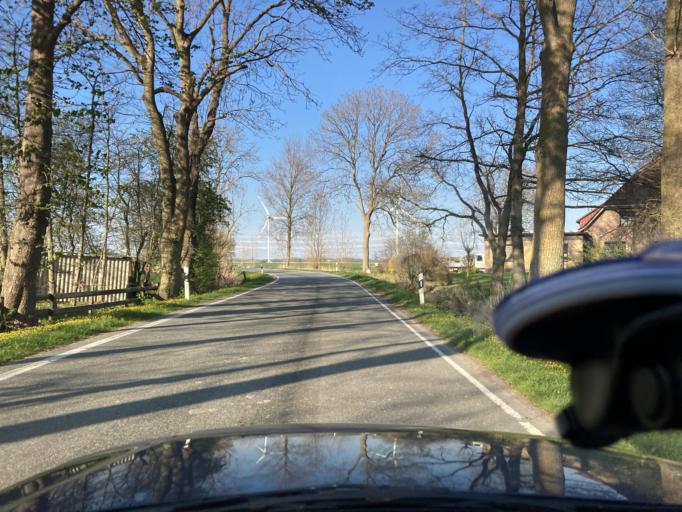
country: DE
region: Schleswig-Holstein
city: Lieth
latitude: 54.1747
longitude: 9.0349
